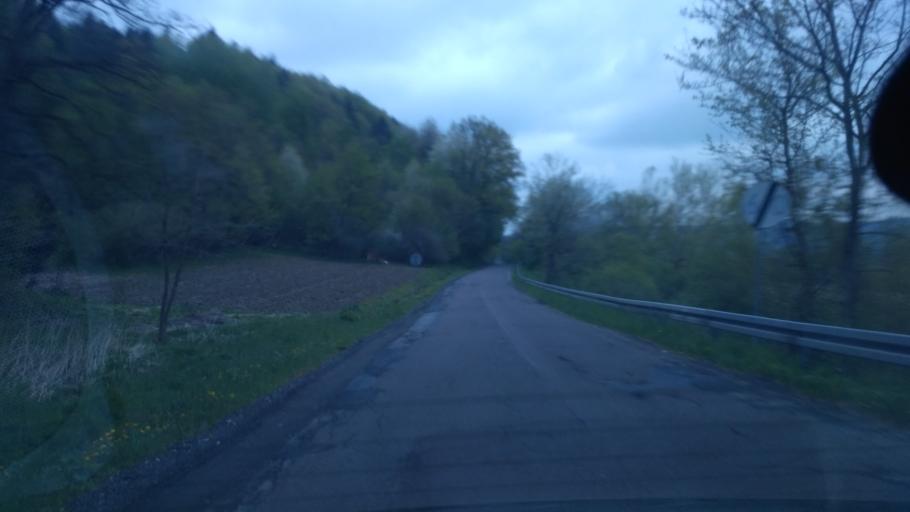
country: PL
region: Subcarpathian Voivodeship
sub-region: Powiat brzozowski
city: Nozdrzec
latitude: 49.7402
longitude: 22.2065
